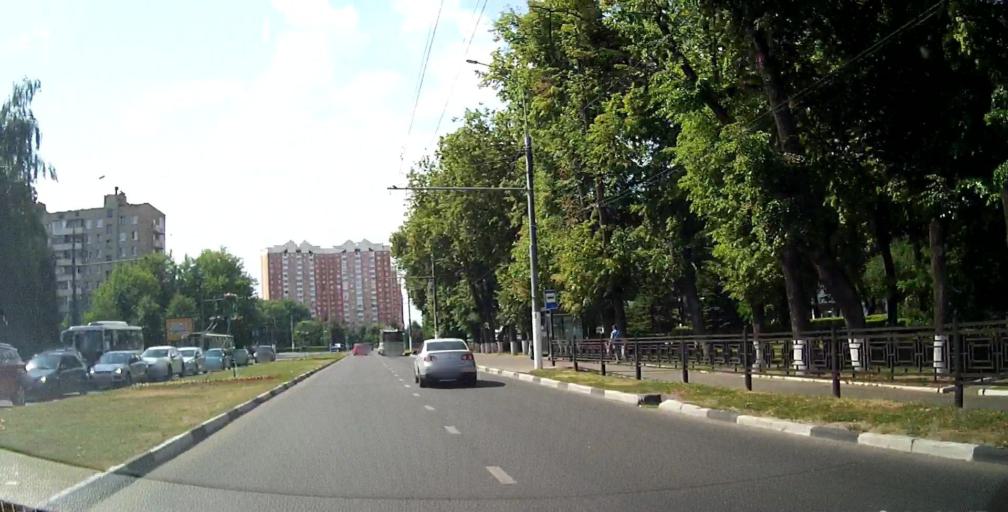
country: RU
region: Moskovskaya
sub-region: Podol'skiy Rayon
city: Podol'sk
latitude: 55.4289
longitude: 37.5436
